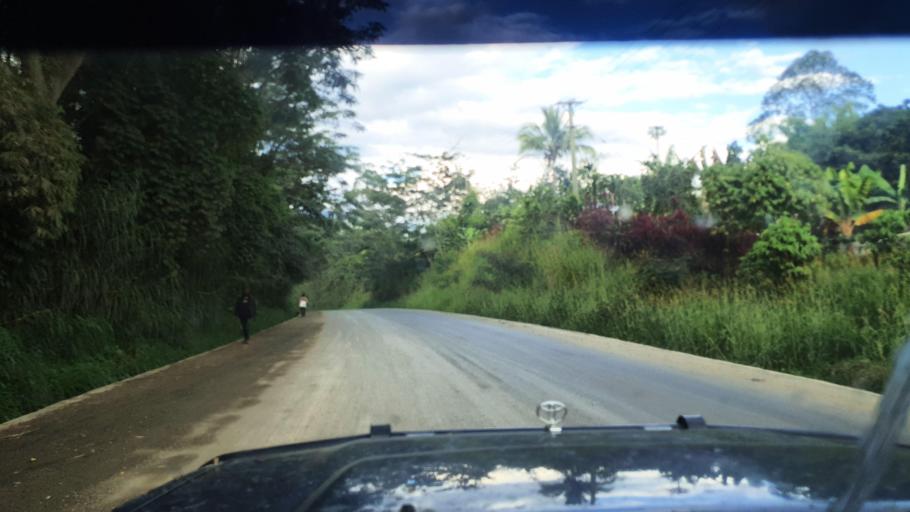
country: PG
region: Jiwaka
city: Minj
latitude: -5.9437
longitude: 144.8208
